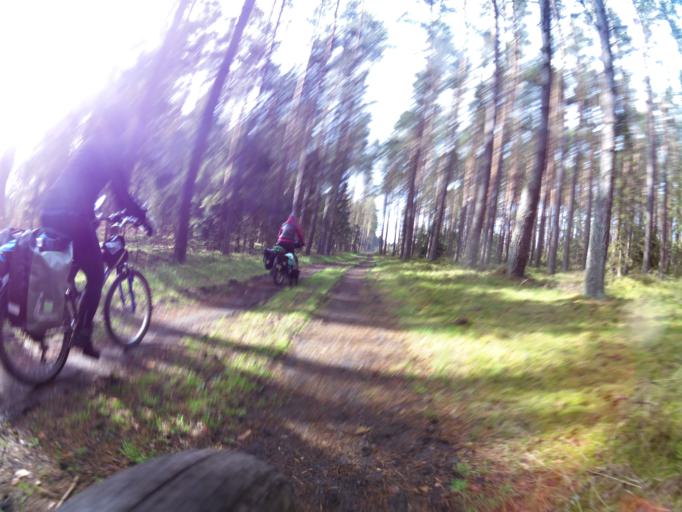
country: PL
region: Pomeranian Voivodeship
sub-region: Powiat slupski
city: Kepice
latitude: 54.2952
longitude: 16.8358
